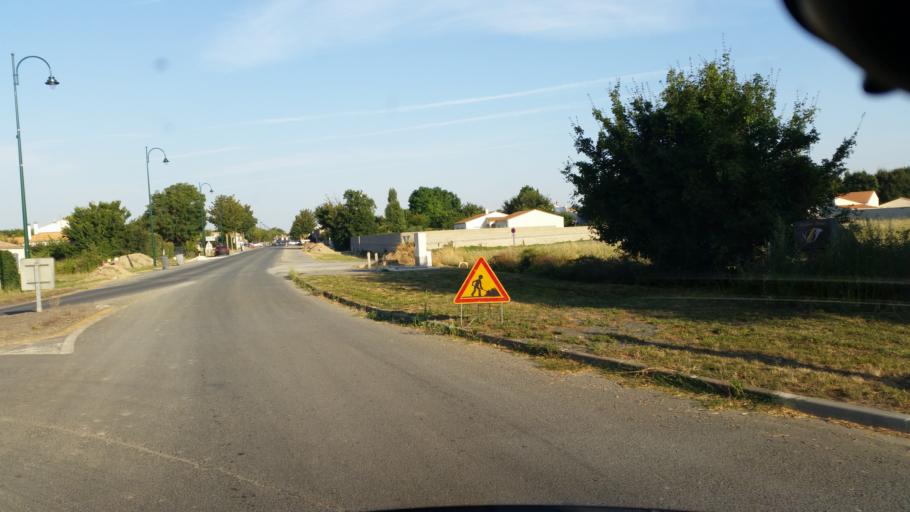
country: FR
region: Poitou-Charentes
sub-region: Departement de la Charente-Maritime
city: Courcon
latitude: 46.2264
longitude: -0.8521
